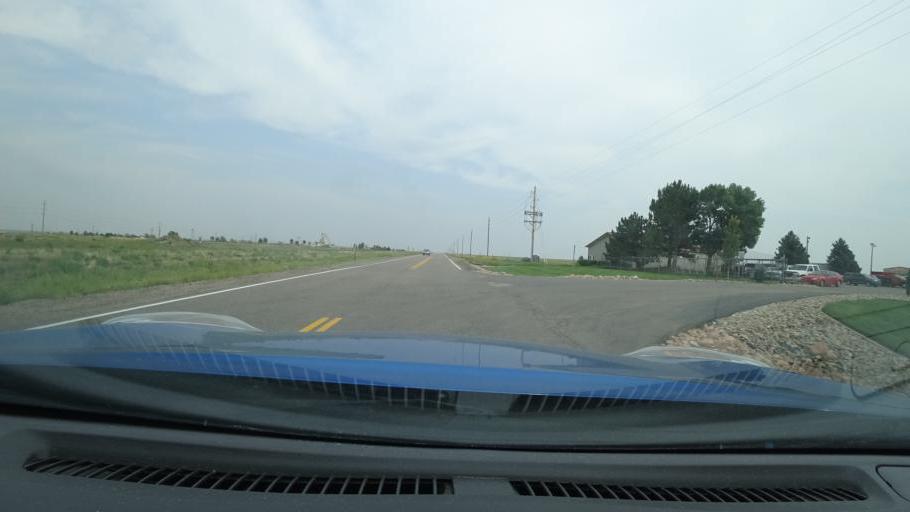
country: US
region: Colorado
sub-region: Adams County
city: Aurora
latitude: 39.7515
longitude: -104.7471
